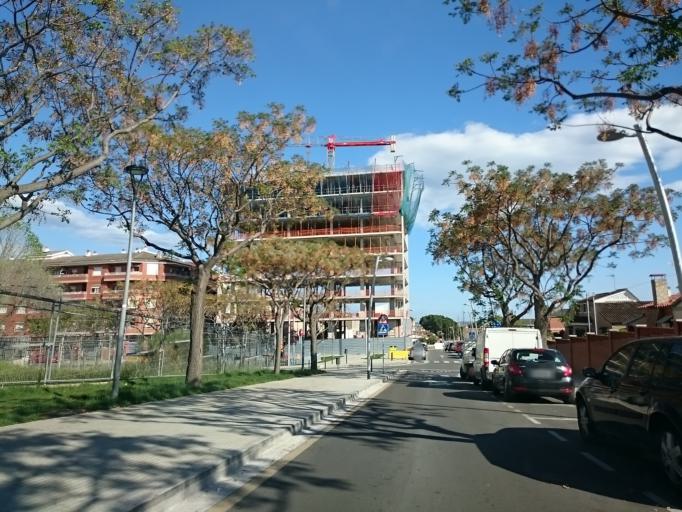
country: ES
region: Catalonia
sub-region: Provincia de Barcelona
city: Viladecans
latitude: 41.3167
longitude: 2.0050
